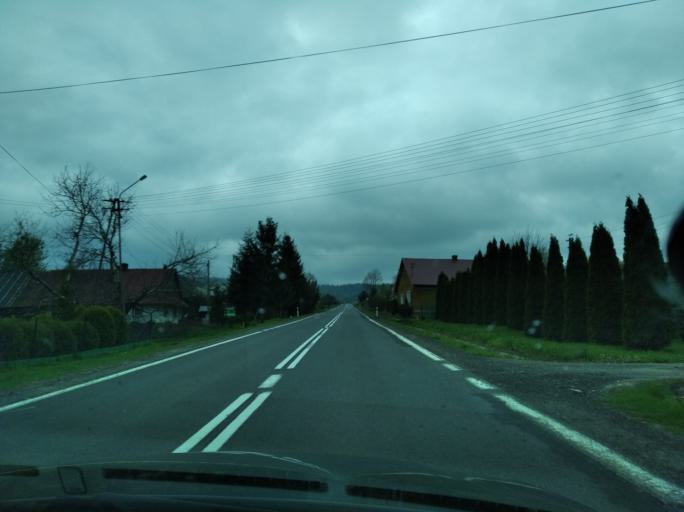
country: PL
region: Subcarpathian Voivodeship
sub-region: Powiat sanocki
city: Tyrawa Woloska
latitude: 49.5754
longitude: 22.3631
